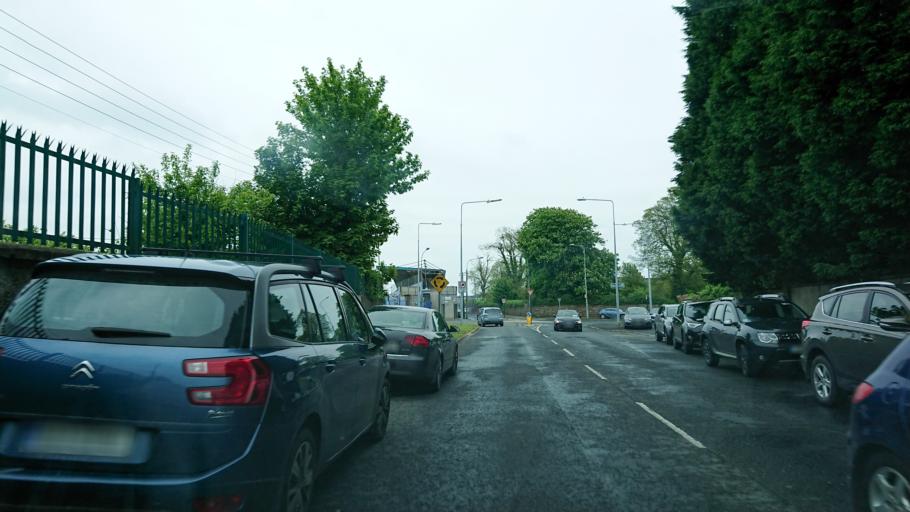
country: IE
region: Munster
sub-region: Waterford
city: Waterford
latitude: 52.2539
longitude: -7.1311
